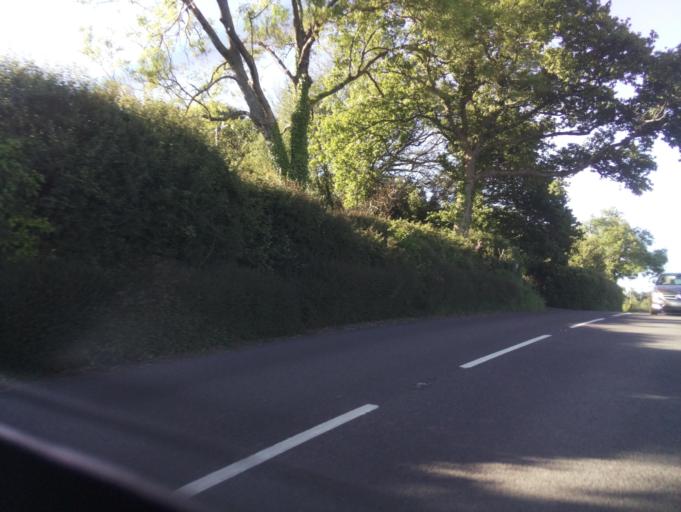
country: GB
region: England
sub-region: Dorset
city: Lyme Regis
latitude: 50.8007
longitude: -2.8669
